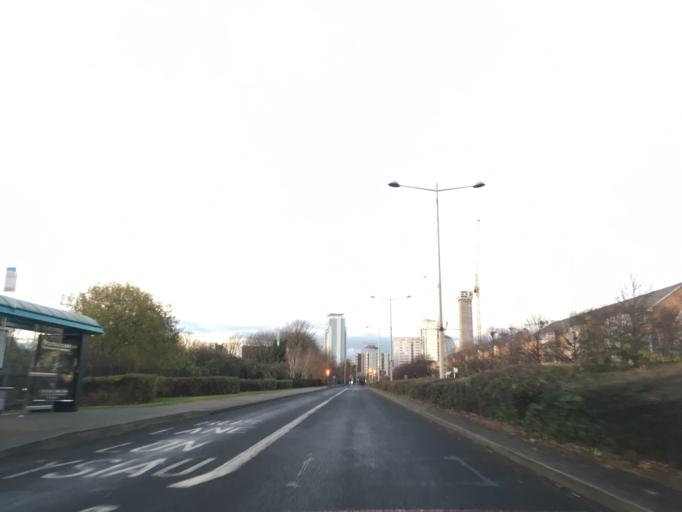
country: GB
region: Wales
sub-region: Cardiff
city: Cardiff
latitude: 51.4721
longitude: -3.1697
